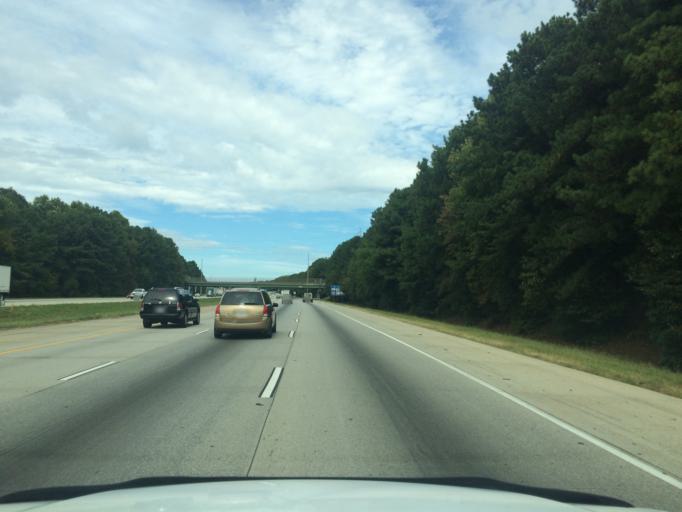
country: US
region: Georgia
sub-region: Cobb County
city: Kennesaw
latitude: 34.0471
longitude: -84.5840
